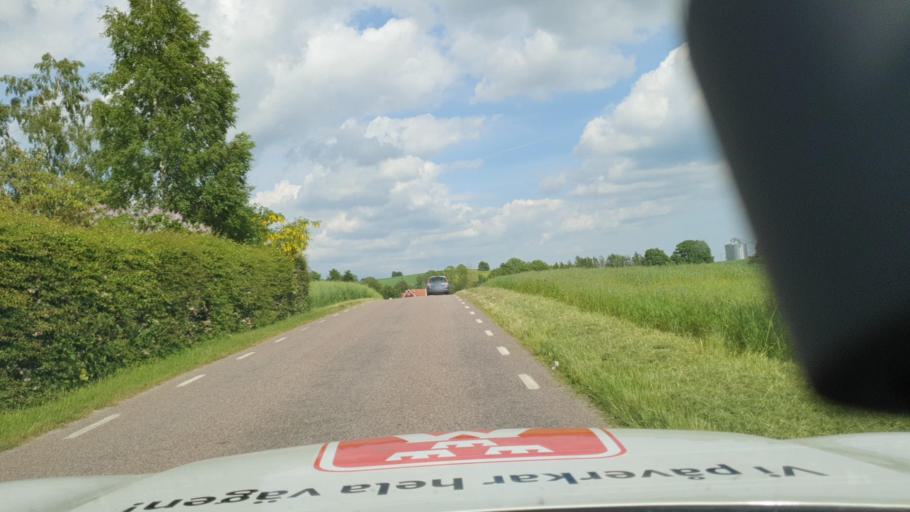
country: SE
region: Skane
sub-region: Skurups Kommun
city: Skurup
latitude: 55.5158
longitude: 13.5246
